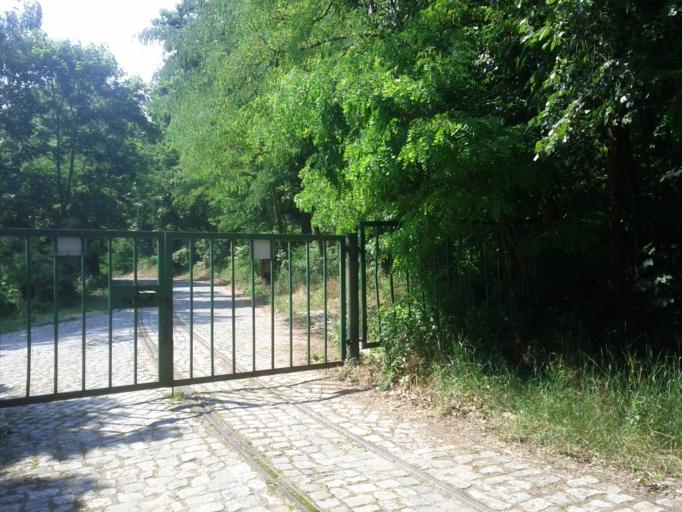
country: DE
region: Brandenburg
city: Woltersdorf
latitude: 52.4735
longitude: 13.7892
